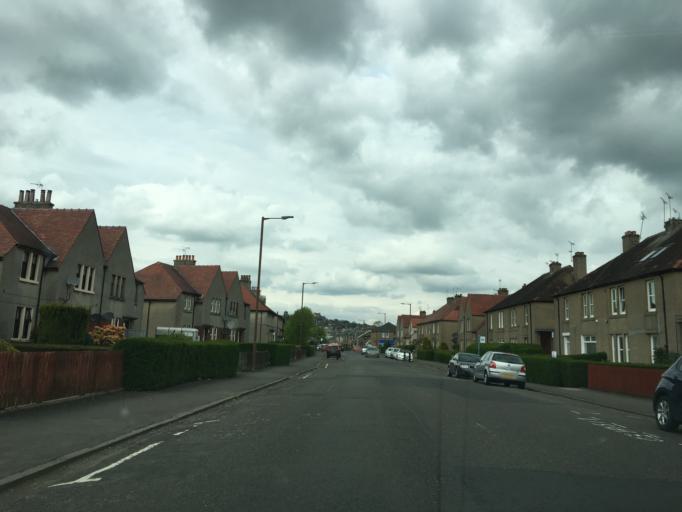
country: GB
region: Scotland
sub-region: Stirling
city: Stirling
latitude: 56.1102
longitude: -3.9292
